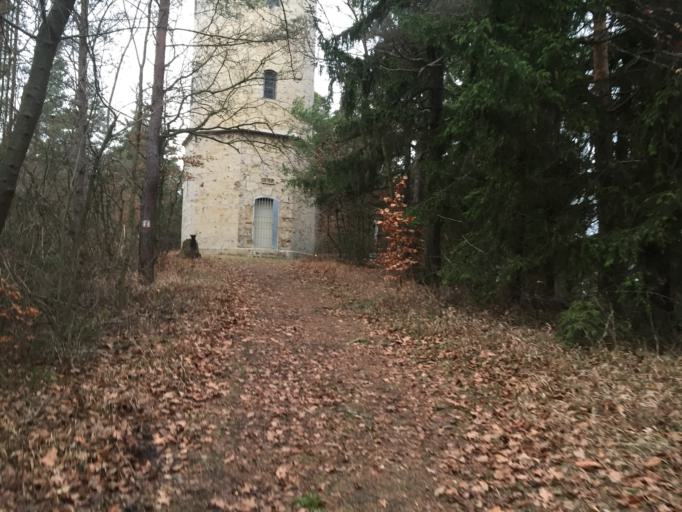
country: DE
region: Thuringia
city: Bad Blankenburg
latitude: 50.7087
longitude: 11.2314
